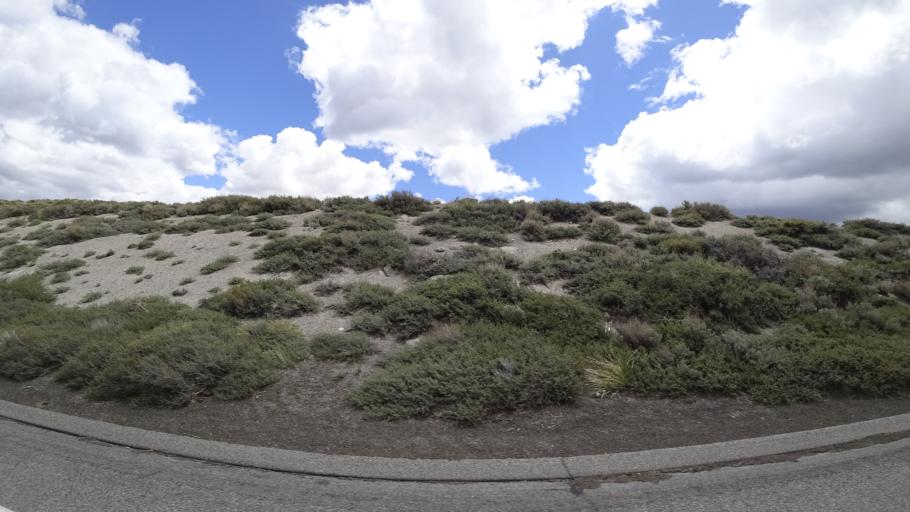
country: US
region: California
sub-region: Mono County
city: Bridgeport
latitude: 38.0763
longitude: -119.1715
